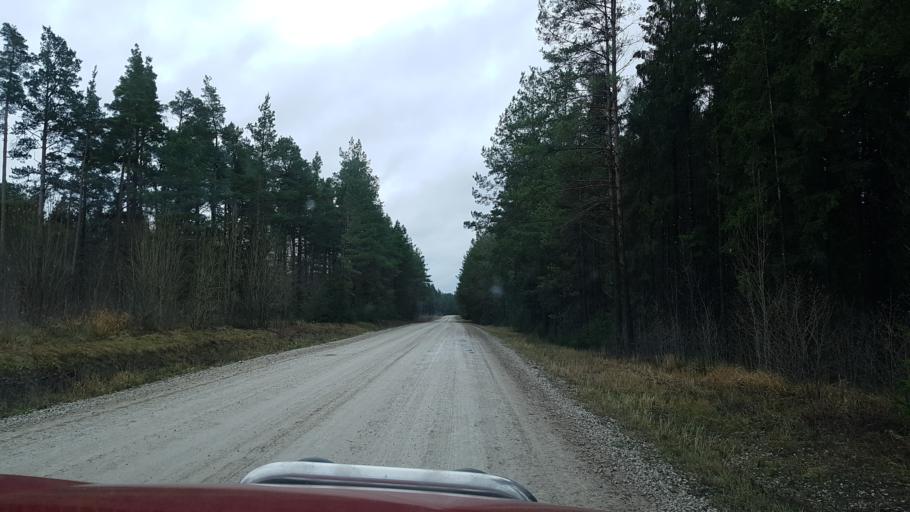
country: EE
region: Paernumaa
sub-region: Halinga vald
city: Parnu-Jaagupi
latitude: 58.5508
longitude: 24.4118
